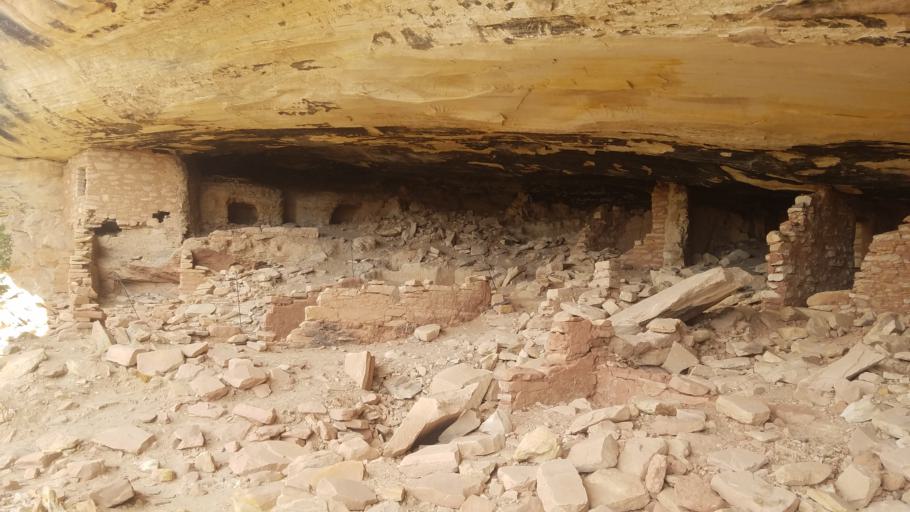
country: US
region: Utah
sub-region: San Juan County
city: Blanding
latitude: 37.4281
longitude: -109.6395
